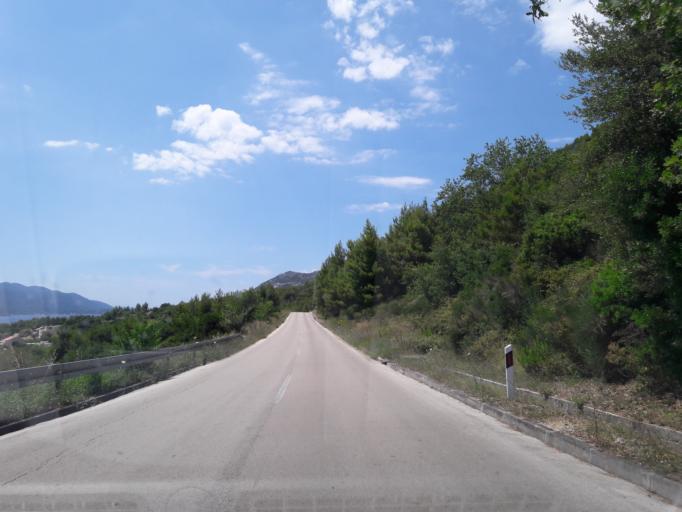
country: HR
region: Dubrovacko-Neretvanska
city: Korcula
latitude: 42.9820
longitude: 17.1175
